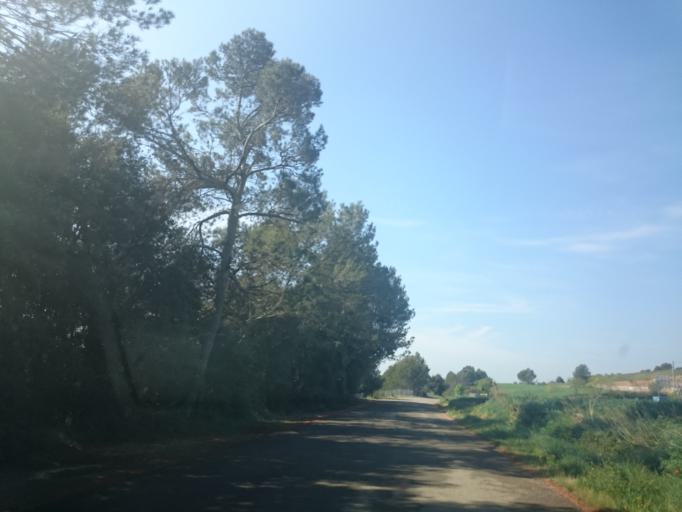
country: ES
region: Catalonia
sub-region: Provincia de Girona
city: Cervia de Ter
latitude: 42.0957
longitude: 2.8949
